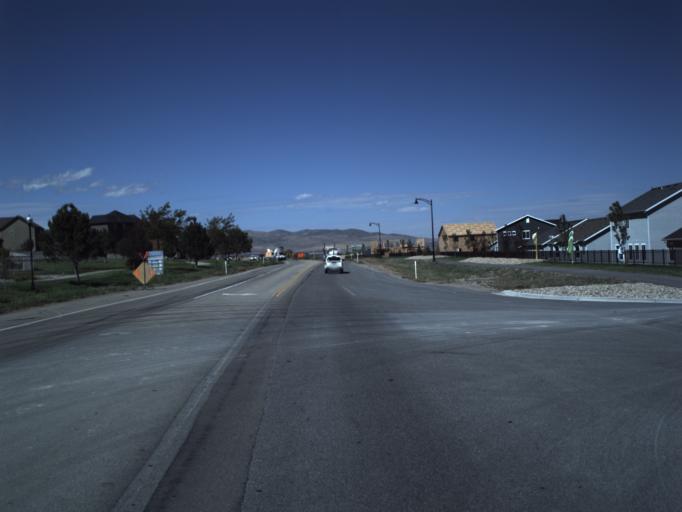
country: US
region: Utah
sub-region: Utah County
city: Saratoga Springs
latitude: 40.3123
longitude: -111.8922
